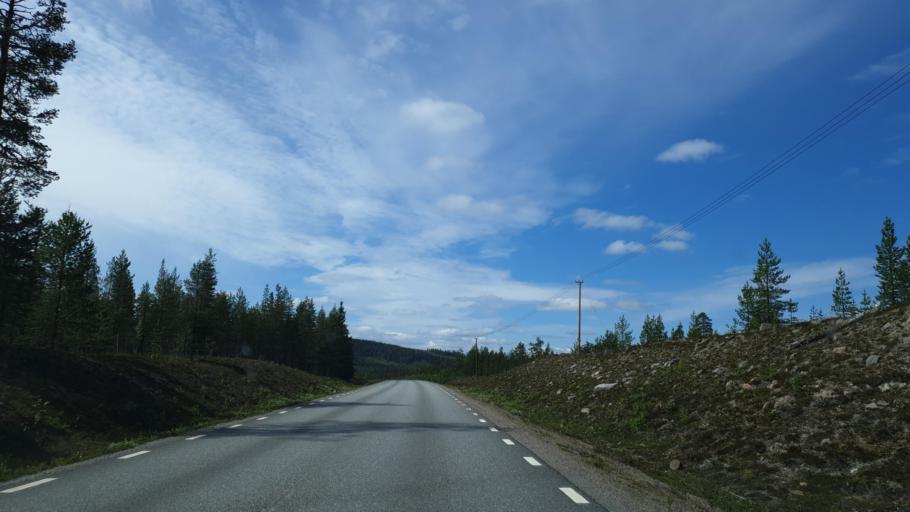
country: SE
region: Vaesterbotten
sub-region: Mala Kommun
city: Mala
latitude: 65.6123
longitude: 18.6770
